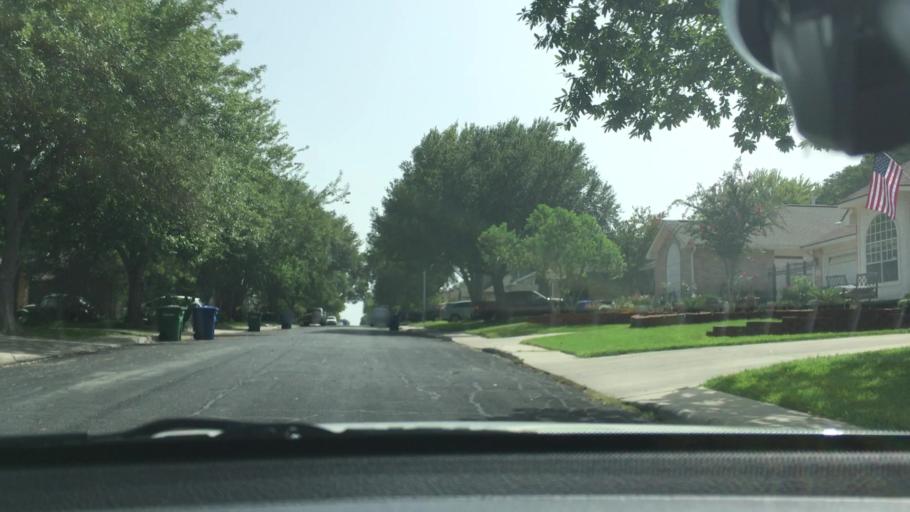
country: US
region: Texas
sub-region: Bexar County
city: Live Oak
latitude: 29.5785
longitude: -98.3802
